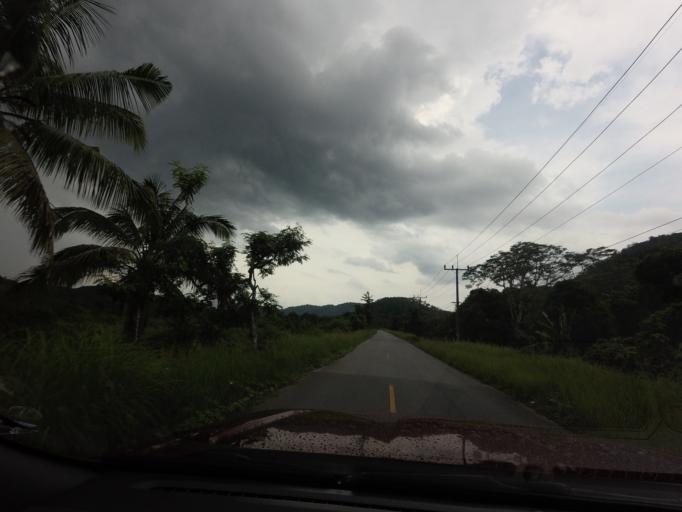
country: TH
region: Yala
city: Ban Nang Sata
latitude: 6.2228
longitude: 101.2268
